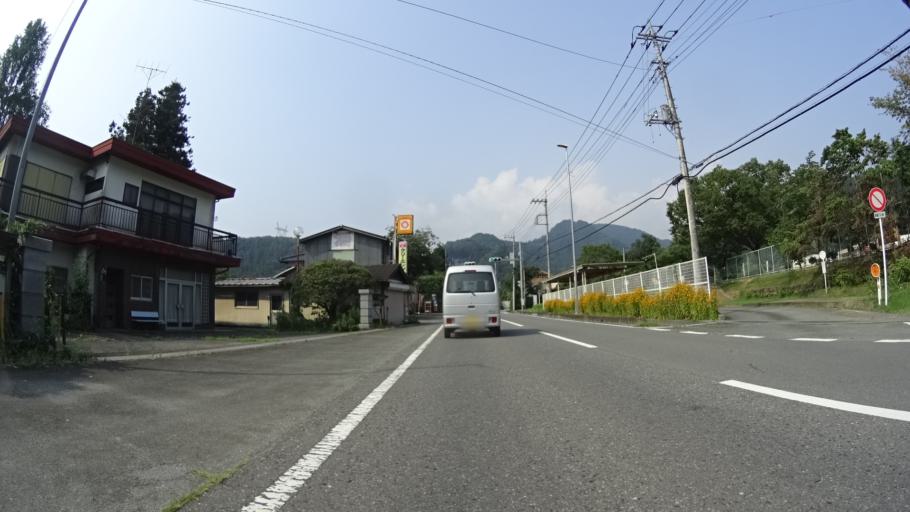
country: JP
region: Saitama
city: Chichibu
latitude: 36.0268
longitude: 138.9702
